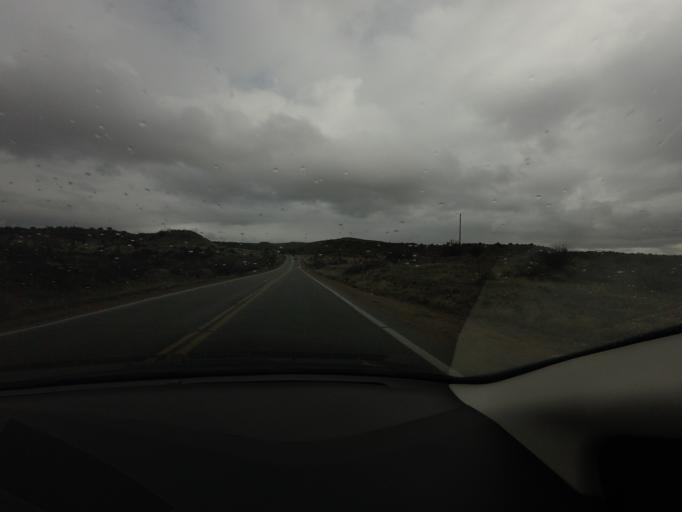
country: US
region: Arizona
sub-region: Yavapai County
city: Cornville
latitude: 34.7073
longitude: -111.8763
